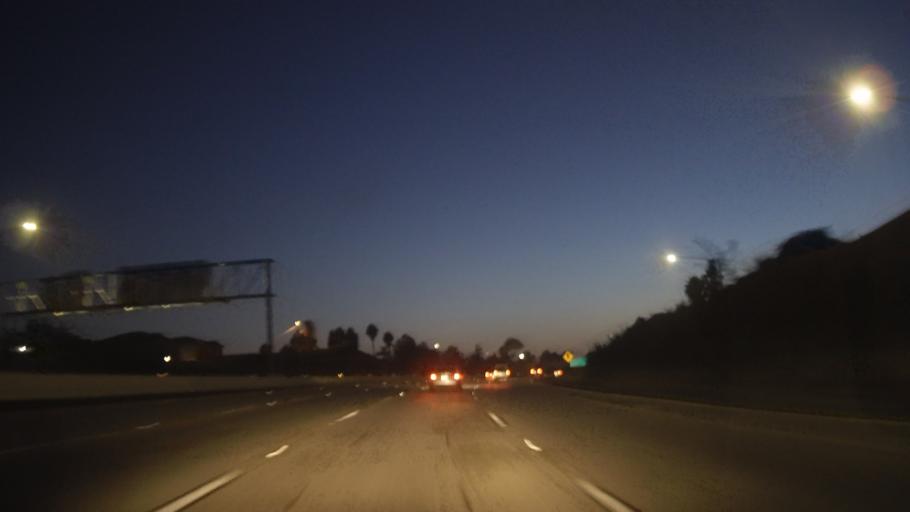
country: US
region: California
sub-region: San Diego County
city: Lemon Grove
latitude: 32.7475
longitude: -117.0208
